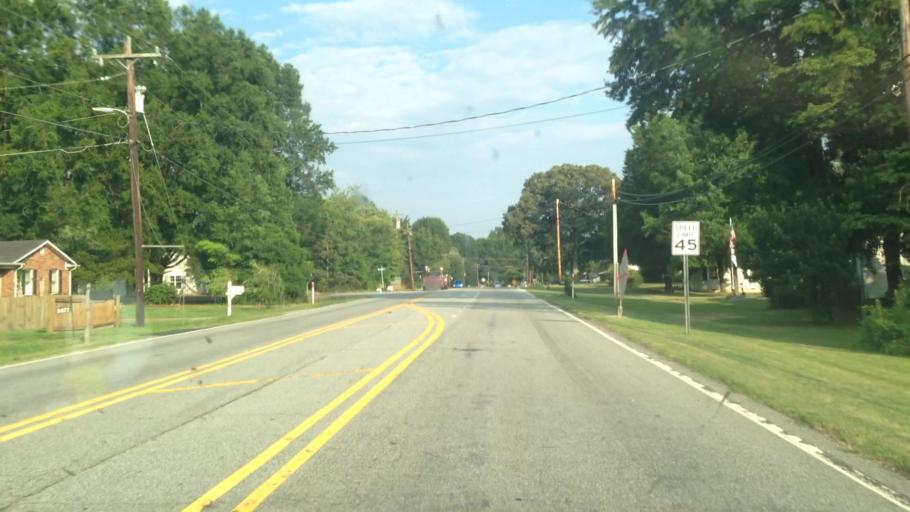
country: US
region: North Carolina
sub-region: Forsyth County
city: Kernersville
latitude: 36.0431
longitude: -80.0542
